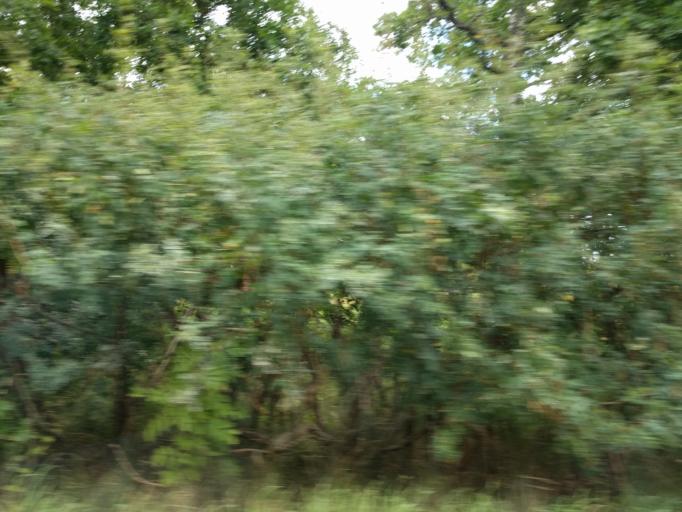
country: SE
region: Soedermanland
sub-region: Oxelosunds Kommun
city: Bara
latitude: 58.4913
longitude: 16.9343
